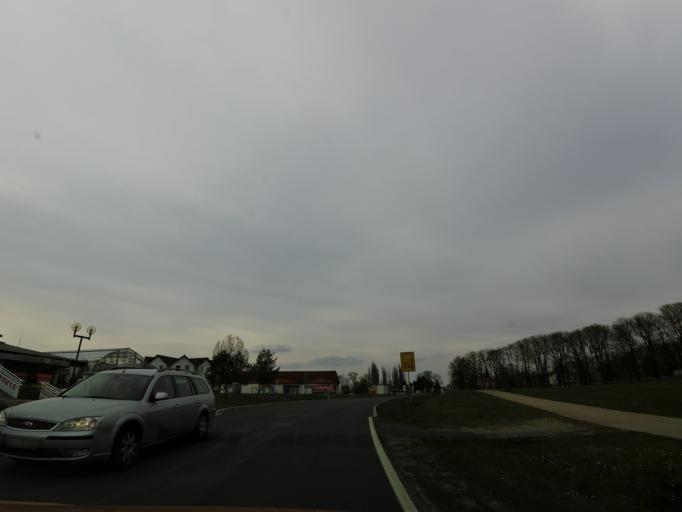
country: DE
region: Brandenburg
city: Rietz Neuendorf
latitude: 52.2021
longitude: 14.1137
